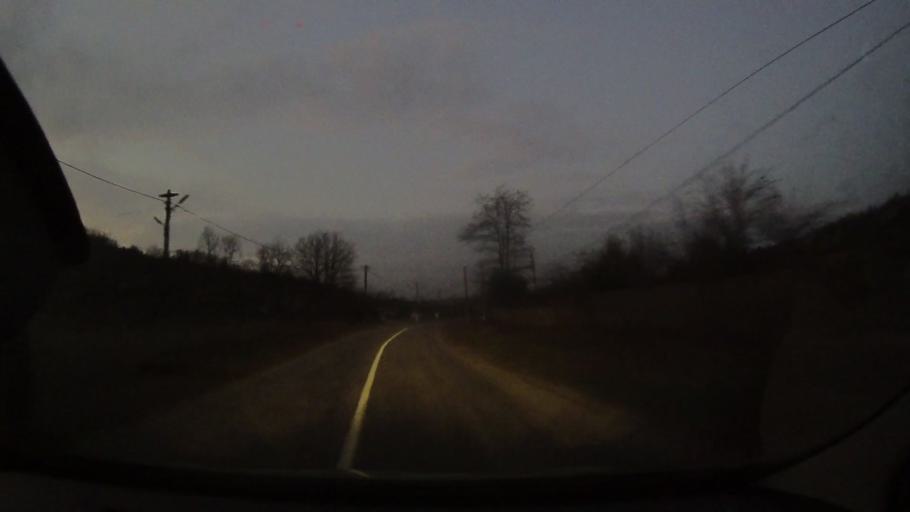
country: RO
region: Constanta
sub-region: Comuna Ion Corvin
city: Ion Corvin
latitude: 44.1424
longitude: 27.8334
